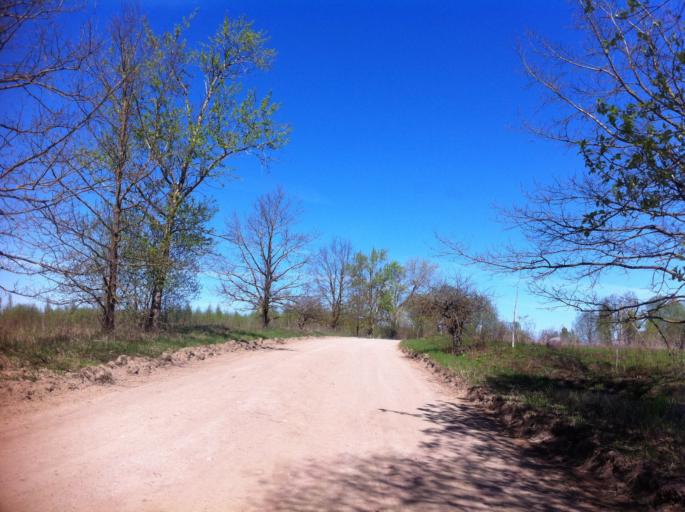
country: RU
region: Pskov
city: Izborsk
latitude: 57.7867
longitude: 27.9627
